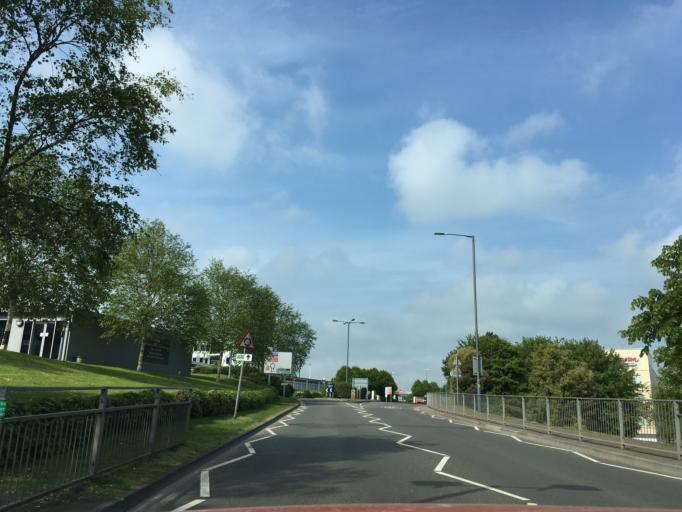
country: GB
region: England
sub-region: North Somerset
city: Butcombe
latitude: 51.3870
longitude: -2.7117
